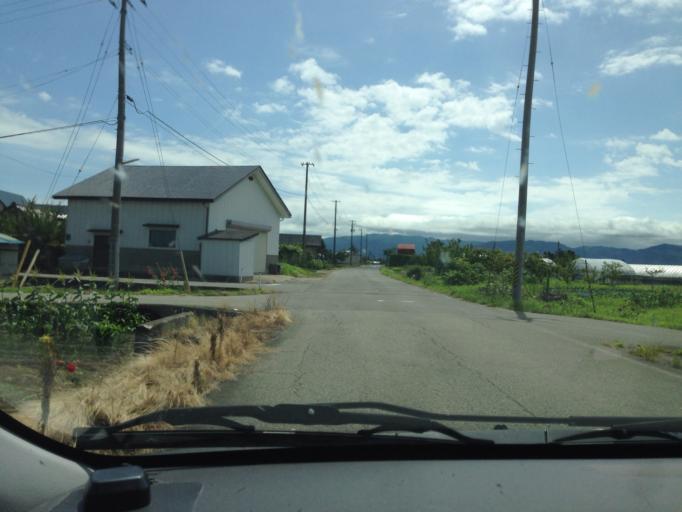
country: JP
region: Fukushima
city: Kitakata
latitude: 37.5143
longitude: 139.8502
